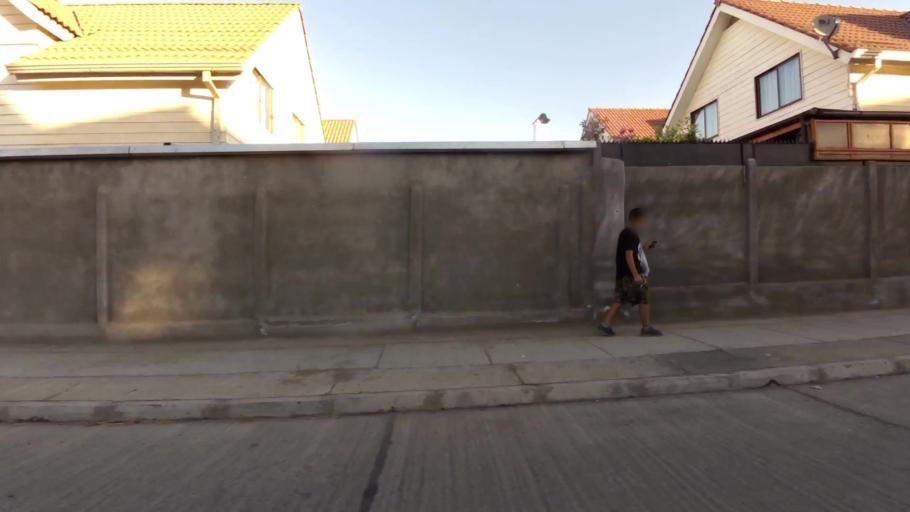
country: CL
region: O'Higgins
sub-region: Provincia de Cachapoal
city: Rancagua
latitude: -34.1882
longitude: -70.7373
